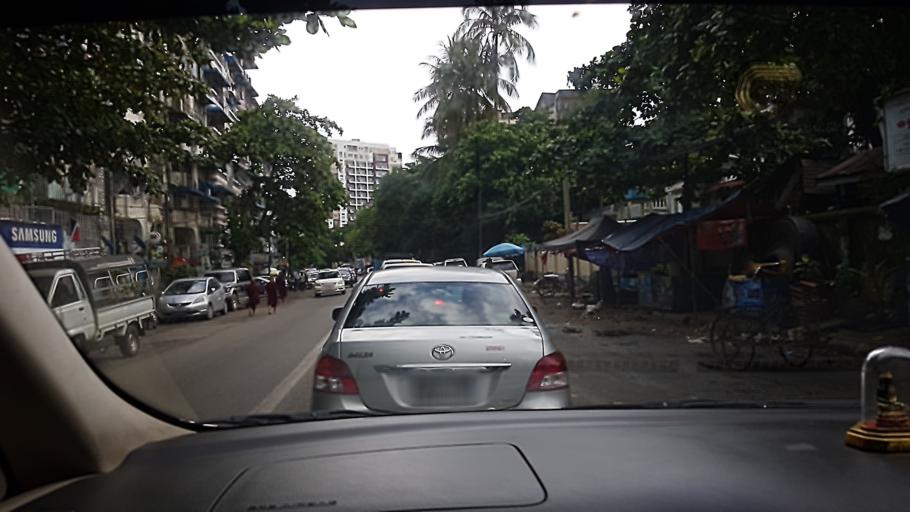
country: MM
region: Yangon
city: Yangon
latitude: 16.8029
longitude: 96.1299
